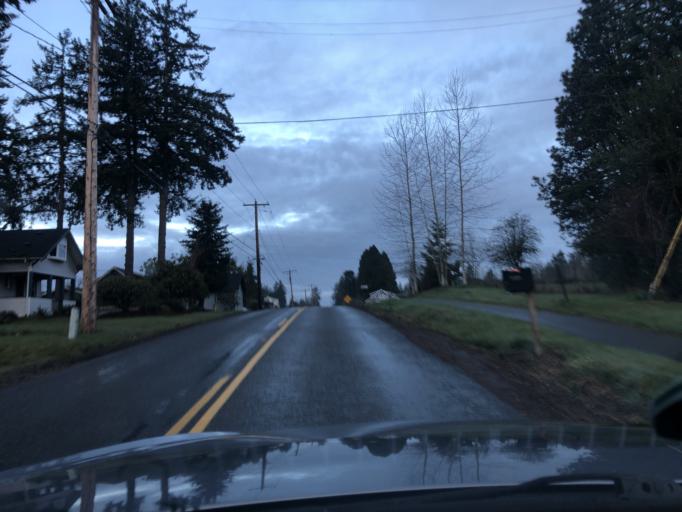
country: US
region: Washington
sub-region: Pierce County
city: North Puyallup
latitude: 47.2249
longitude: -122.2720
